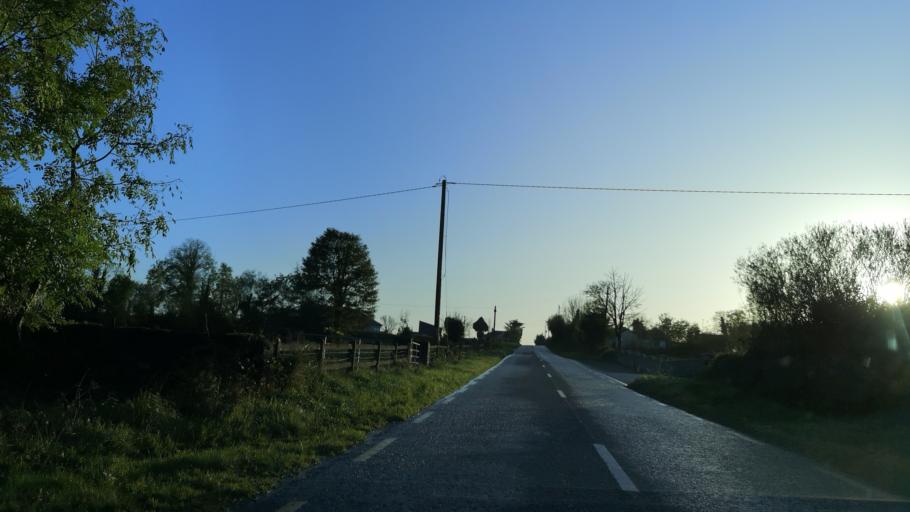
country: IE
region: Connaught
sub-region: Roscommon
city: Castlerea
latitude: 53.7474
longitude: -8.5350
